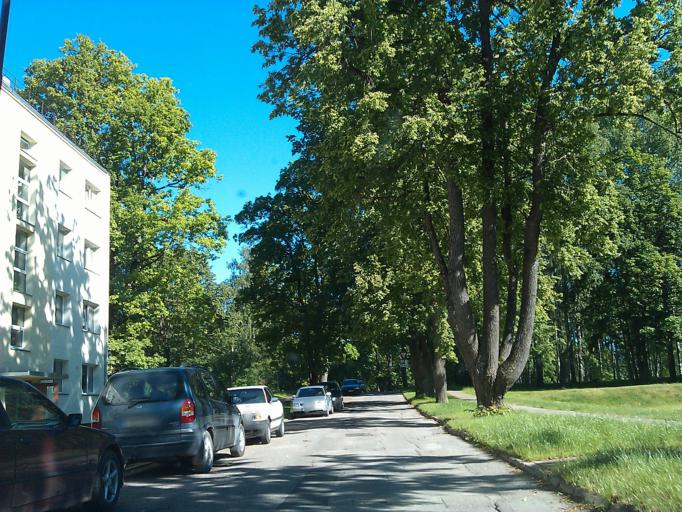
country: LV
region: Cesu Rajons
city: Cesis
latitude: 57.3103
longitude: 25.2492
